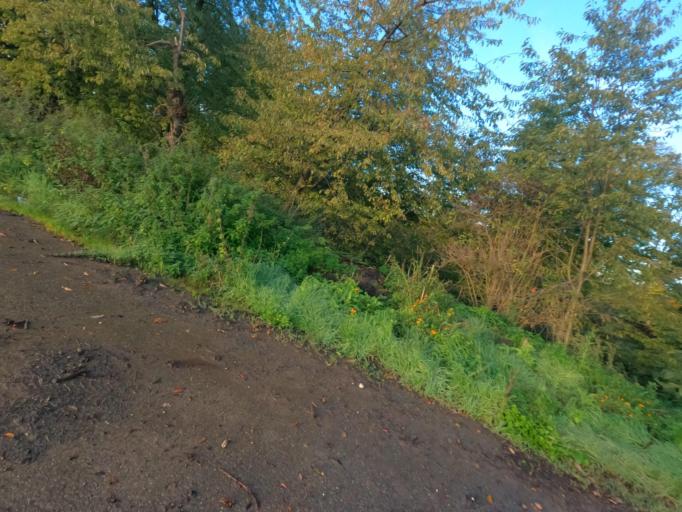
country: DE
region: North Rhine-Westphalia
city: Erkelenz
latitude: 51.0620
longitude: 6.3190
